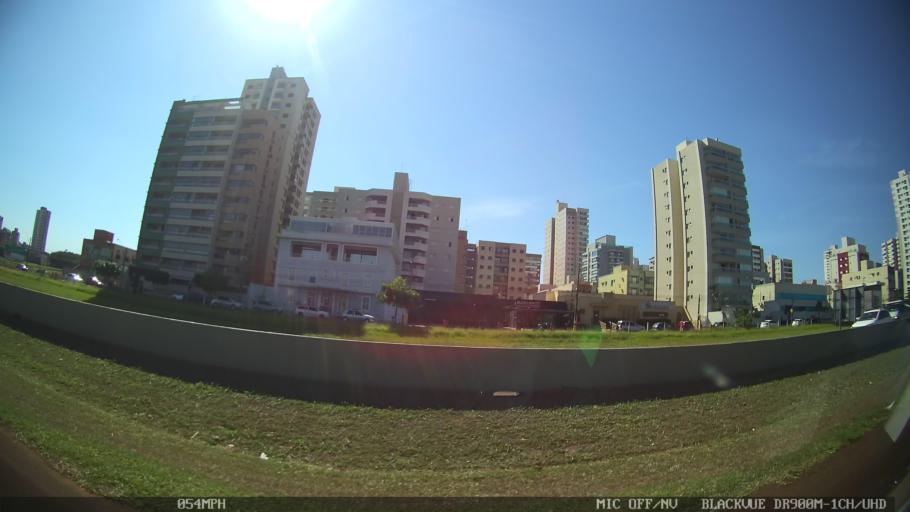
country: BR
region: Sao Paulo
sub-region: Ribeirao Preto
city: Ribeirao Preto
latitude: -21.2211
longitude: -47.8237
